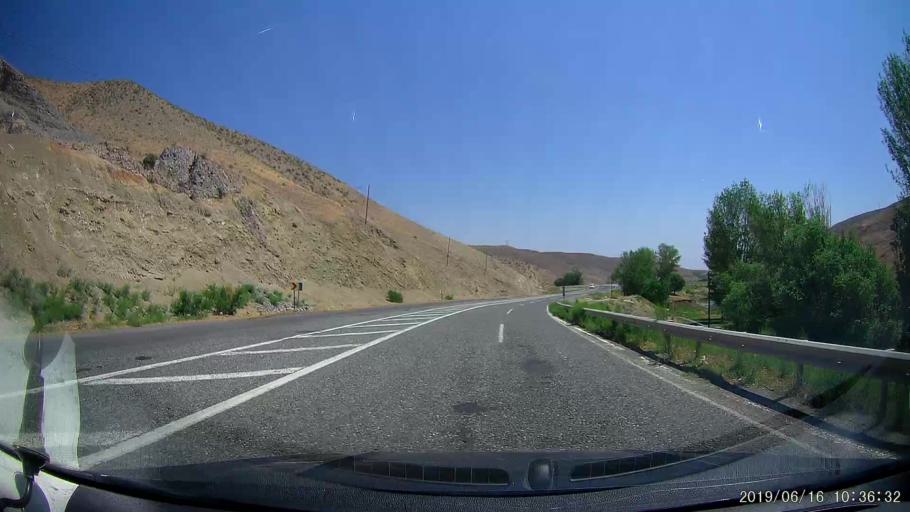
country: TR
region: Igdir
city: Tuzluca
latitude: 40.0393
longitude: 43.6825
